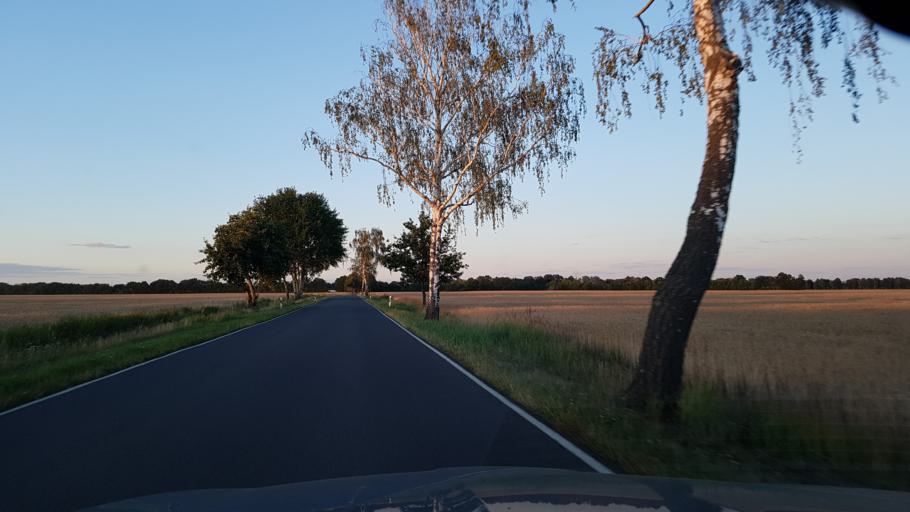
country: DE
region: Brandenburg
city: Plessa
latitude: 51.4252
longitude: 13.6065
